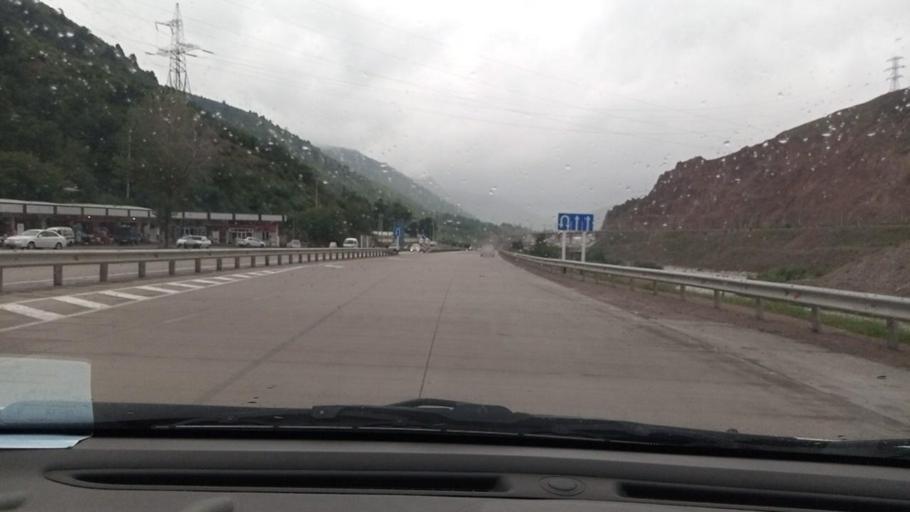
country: UZ
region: Toshkent
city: Angren
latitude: 41.1543
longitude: 70.4442
